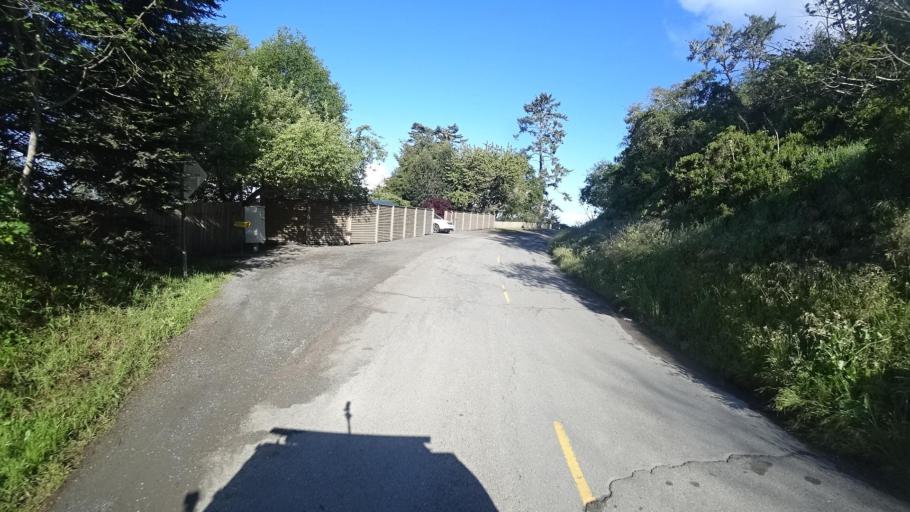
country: US
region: California
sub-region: Humboldt County
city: Westhaven-Moonstone
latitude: 41.0425
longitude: -124.1194
